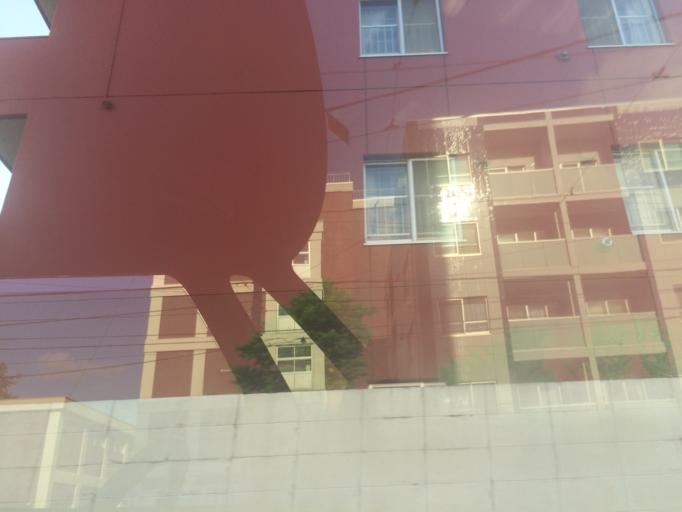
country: JP
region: Hokkaido
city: Sapporo
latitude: 43.0383
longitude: 141.3510
